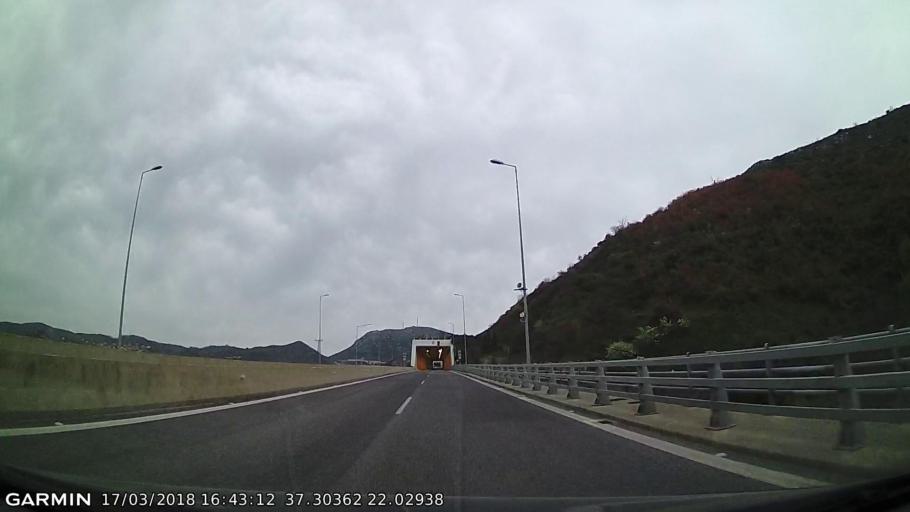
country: GR
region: Peloponnese
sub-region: Nomos Messinias
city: Meligalas
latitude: 37.3042
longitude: 22.0301
